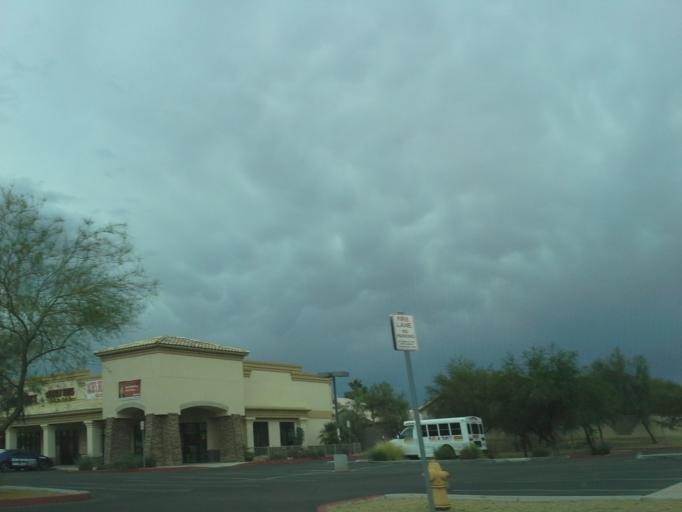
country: US
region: Arizona
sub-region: Maricopa County
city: Paradise Valley
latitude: 33.6415
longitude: -111.9938
